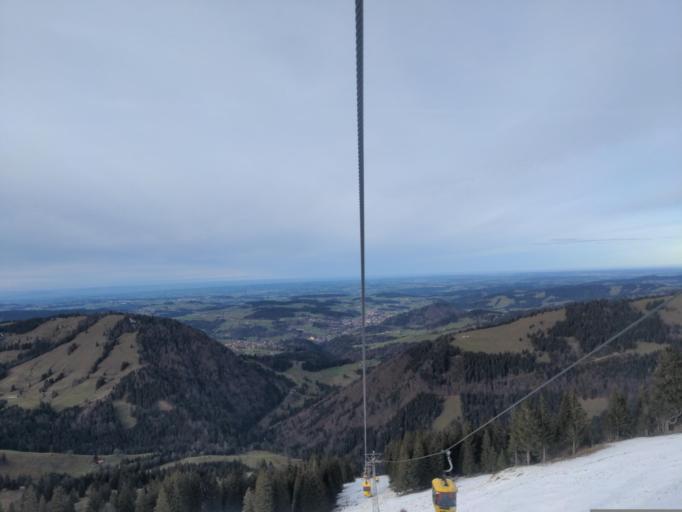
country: DE
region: Bavaria
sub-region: Swabia
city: Balderschwang
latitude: 47.4963
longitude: 10.0692
